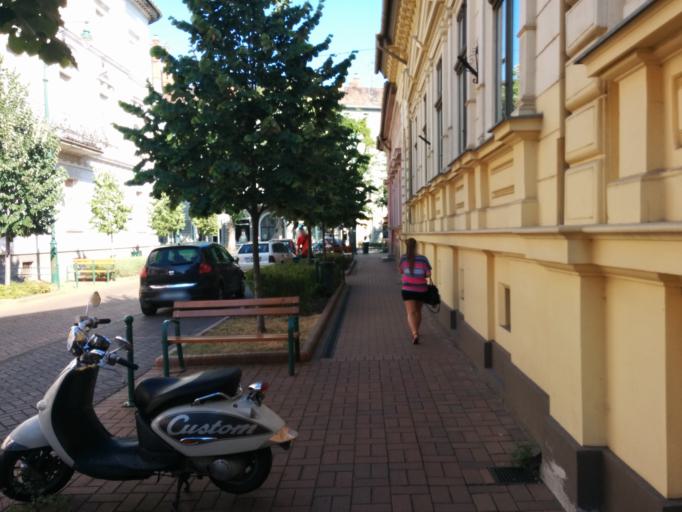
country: HU
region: Csongrad
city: Szeged
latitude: 46.2528
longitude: 20.1444
